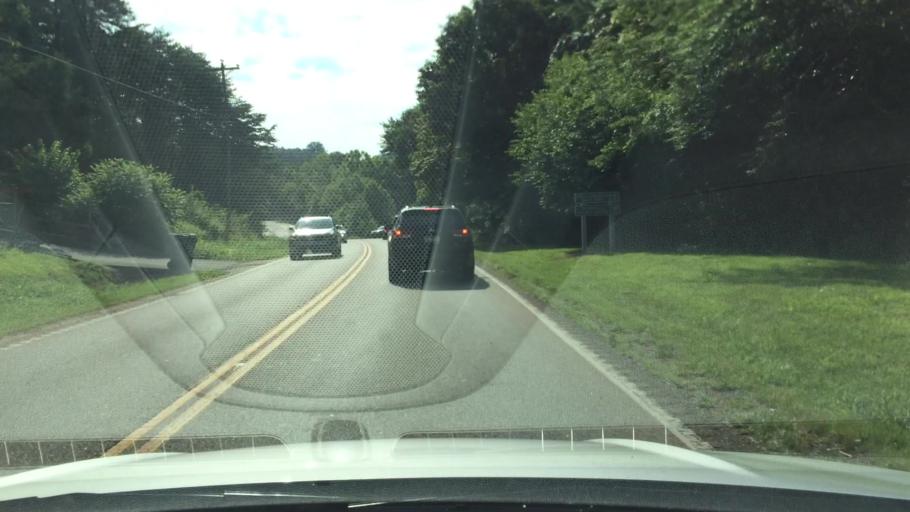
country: US
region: Tennessee
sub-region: Sevier County
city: Sevierville
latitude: 35.9226
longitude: -83.6044
